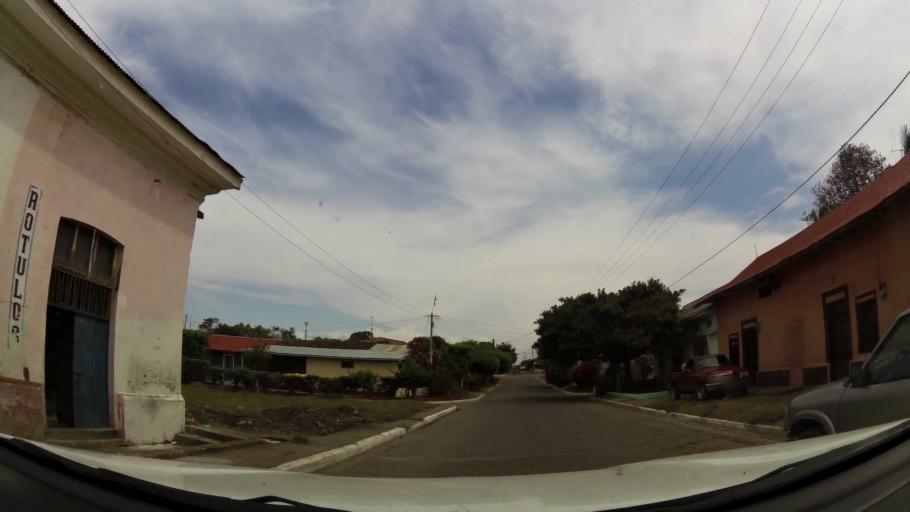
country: NI
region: Rivas
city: Rivas
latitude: 11.4364
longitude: -85.8288
